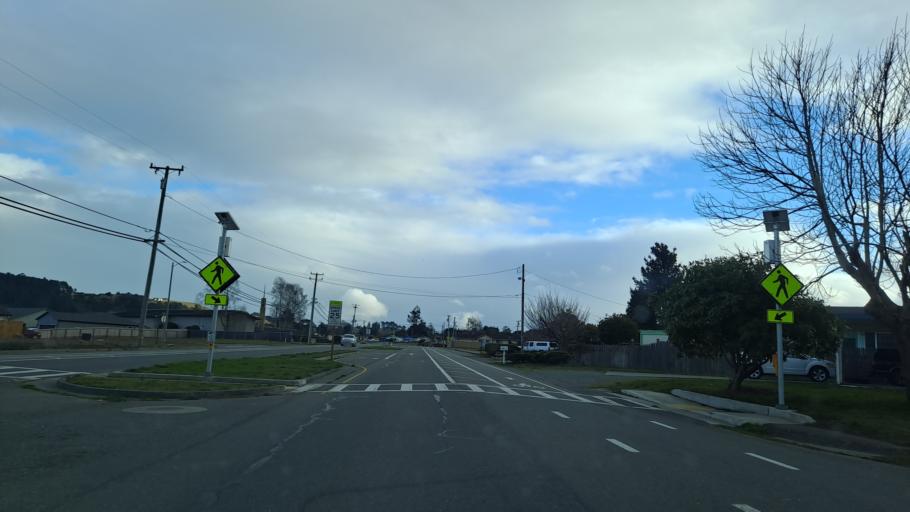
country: US
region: California
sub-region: Humboldt County
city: Fortuna
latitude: 40.5729
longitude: -124.1424
